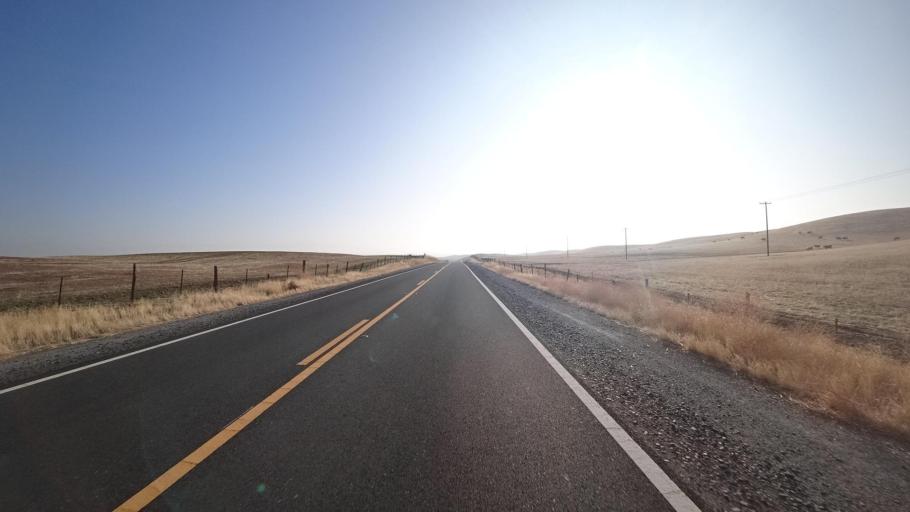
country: US
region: California
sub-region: Tulare County
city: Richgrove
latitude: 35.7544
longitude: -119.0153
